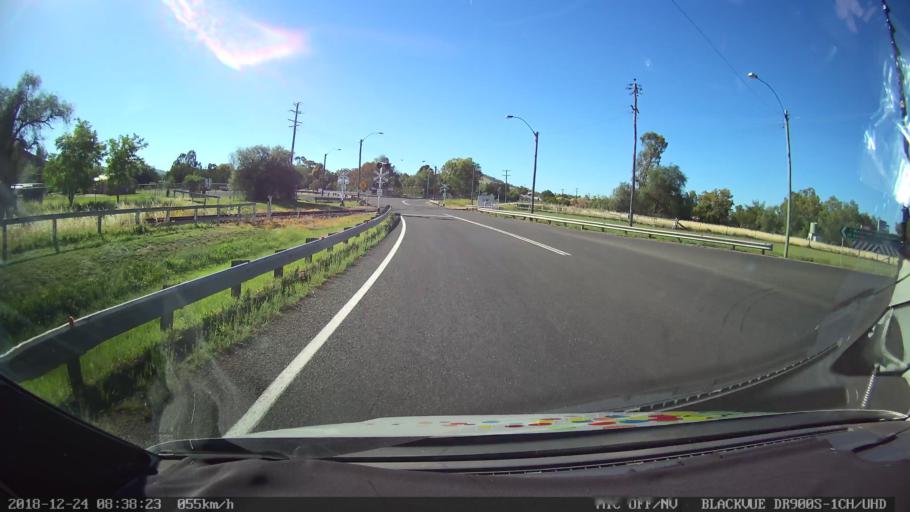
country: AU
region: New South Wales
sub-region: Liverpool Plains
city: Quirindi
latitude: -31.3405
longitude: 150.6475
